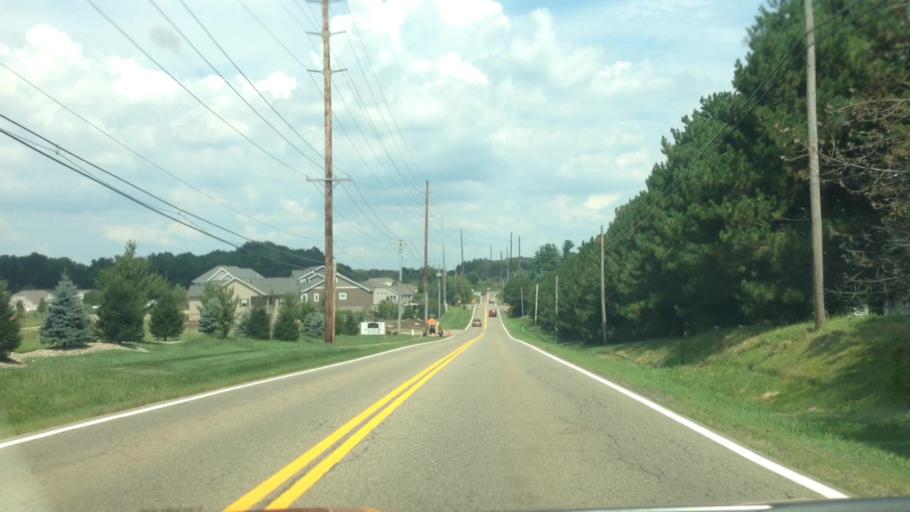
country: US
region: Ohio
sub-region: Stark County
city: Massillon
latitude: 40.8549
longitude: -81.5108
